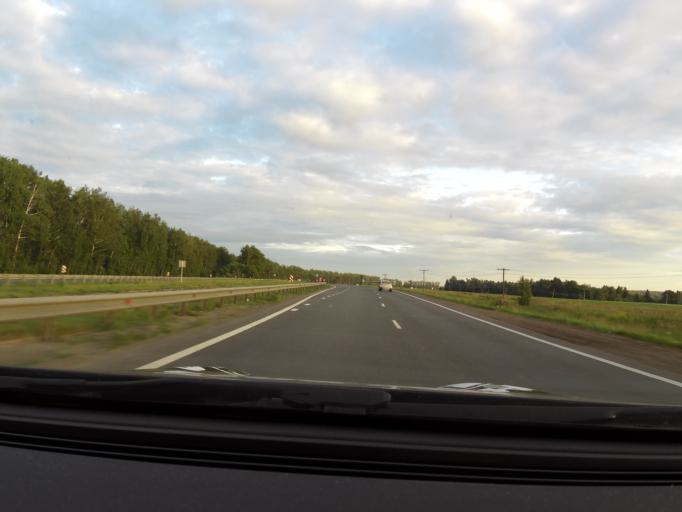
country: RU
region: Chuvashia
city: Ishley
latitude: 56.0874
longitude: 47.0000
